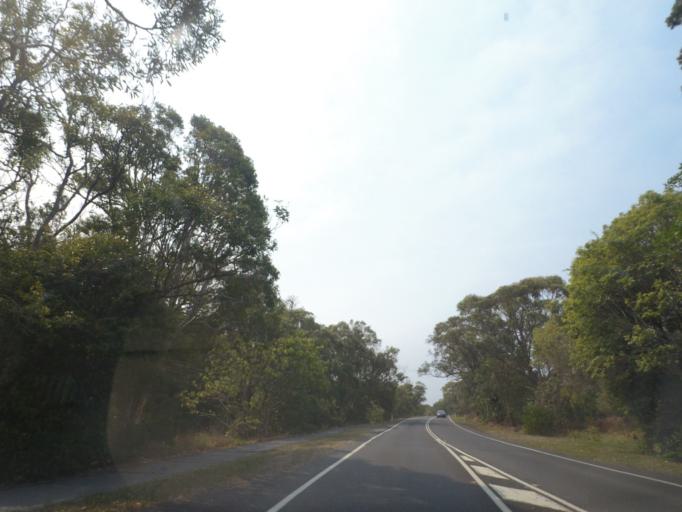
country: AU
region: New South Wales
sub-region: Tweed
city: Pottsville Beach
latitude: -28.3531
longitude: 153.5710
